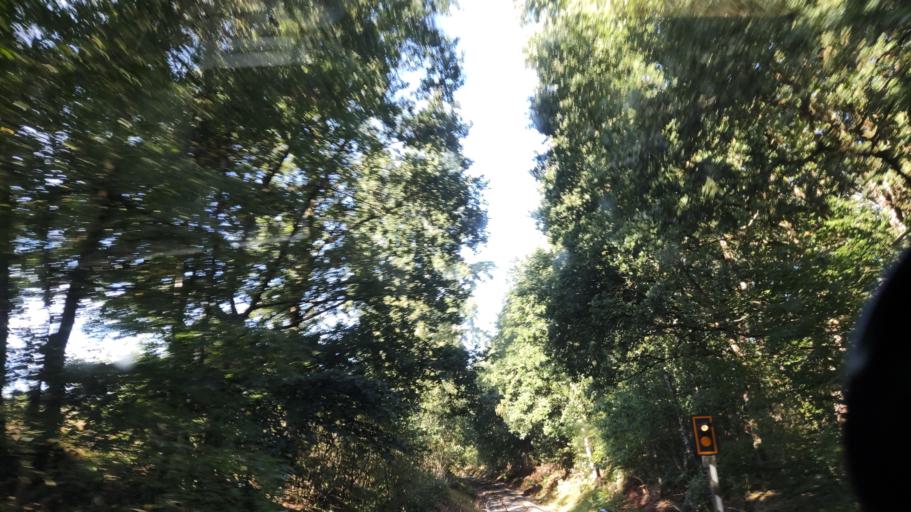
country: DE
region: Lower Saxony
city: Soderstorf
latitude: 53.1399
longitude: 10.1570
